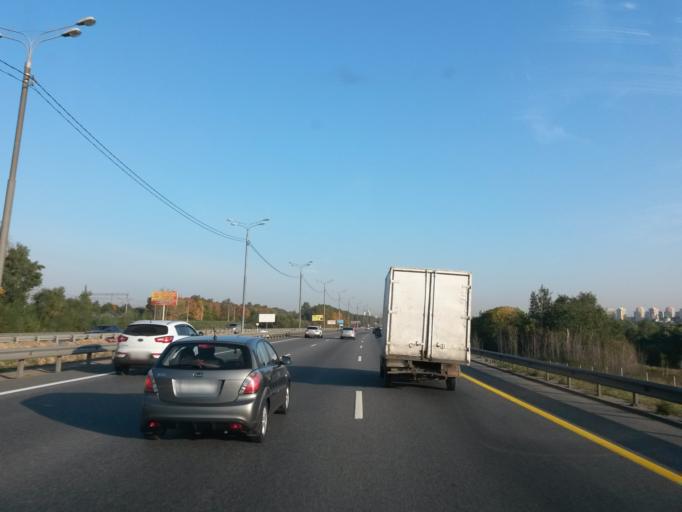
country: RU
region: Moskovskaya
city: Vidnoye
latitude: 55.5240
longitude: 37.7040
